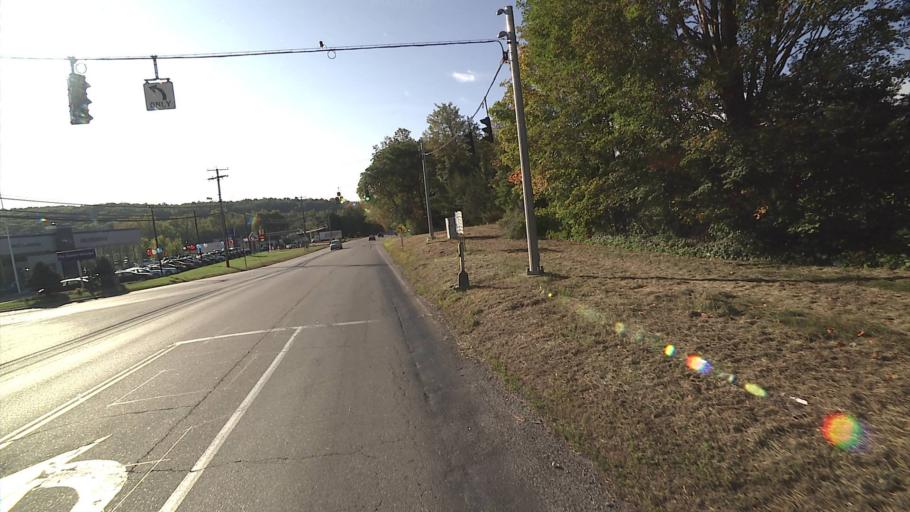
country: US
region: Connecticut
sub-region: New London County
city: Baltic
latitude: 41.5672
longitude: -72.1302
